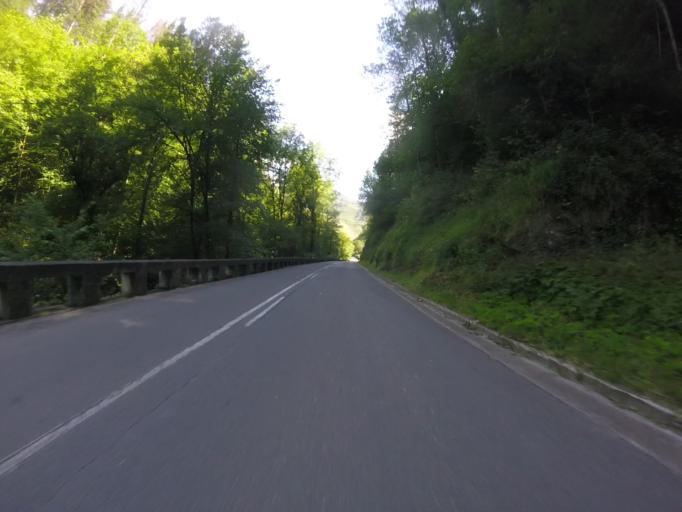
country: ES
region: Basque Country
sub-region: Provincia de Guipuzcoa
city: Beizama
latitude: 43.1015
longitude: -2.2424
